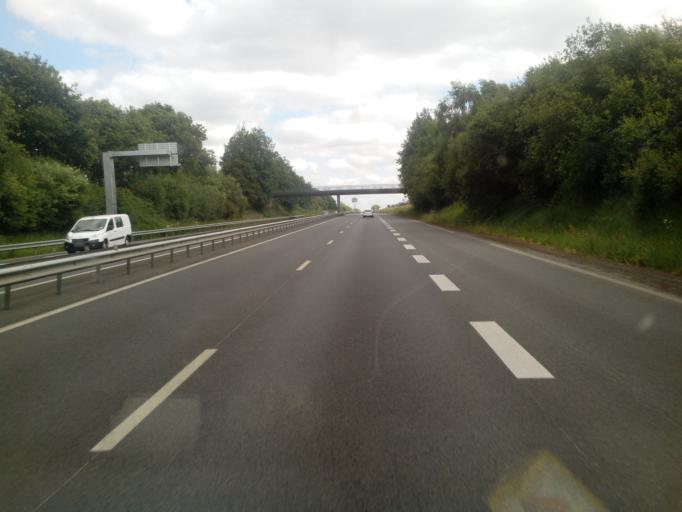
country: FR
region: Brittany
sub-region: Departement des Cotes-d'Armor
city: Broons
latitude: 48.3192
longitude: -2.2501
